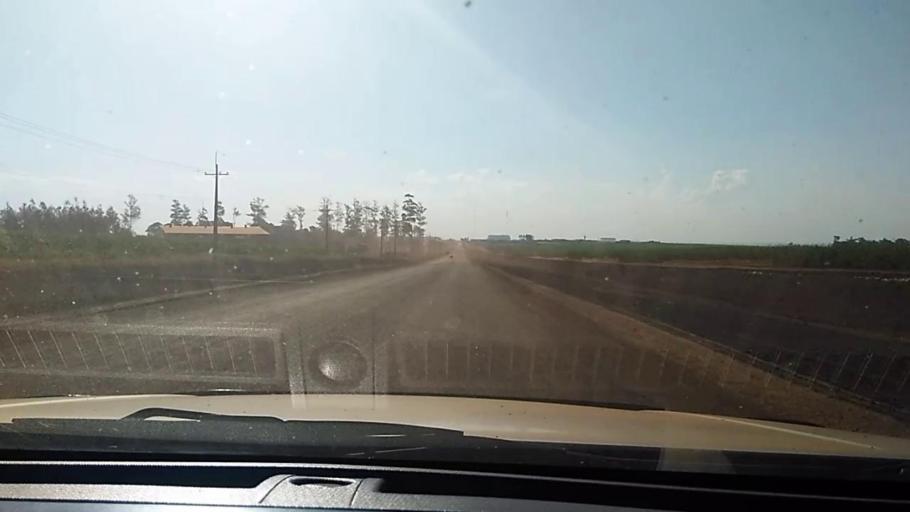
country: PY
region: Alto Parana
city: Naranjal
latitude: -25.9110
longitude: -55.4430
